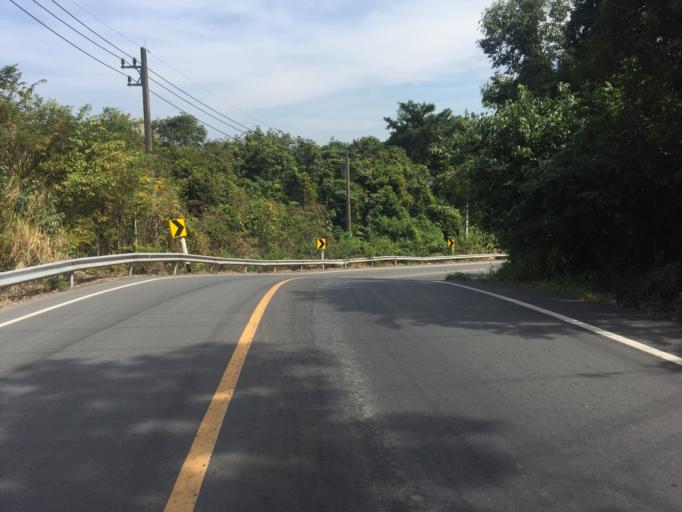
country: TH
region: Trat
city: Laem Ngop
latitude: 12.1416
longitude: 102.2767
